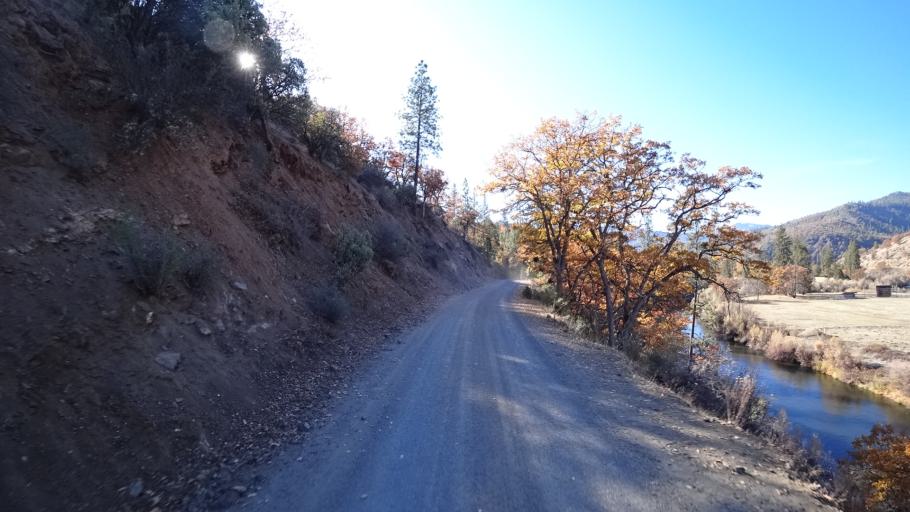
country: US
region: California
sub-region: Siskiyou County
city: Yreka
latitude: 41.8381
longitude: -122.8359
